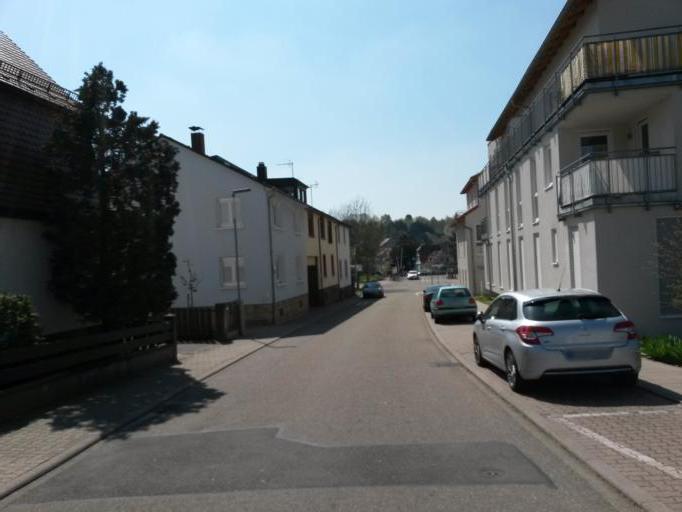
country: DE
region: Baden-Wuerttemberg
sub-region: Karlsruhe Region
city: Joehlingen
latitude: 48.9883
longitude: 8.5448
